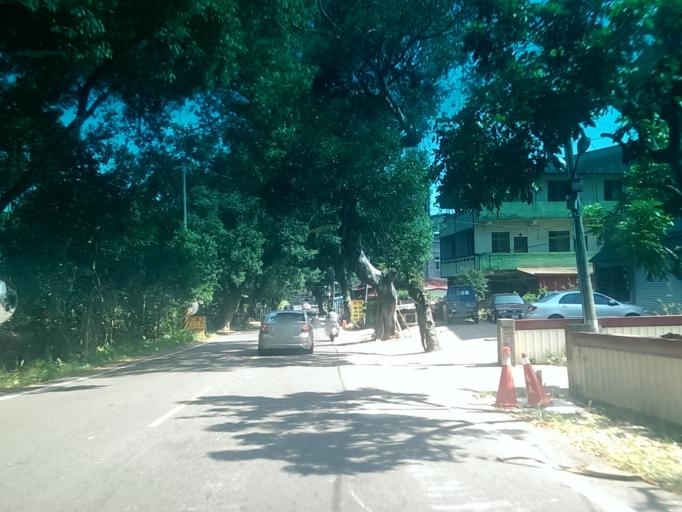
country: TW
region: Taiwan
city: Lugu
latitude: 23.8365
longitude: 120.7337
